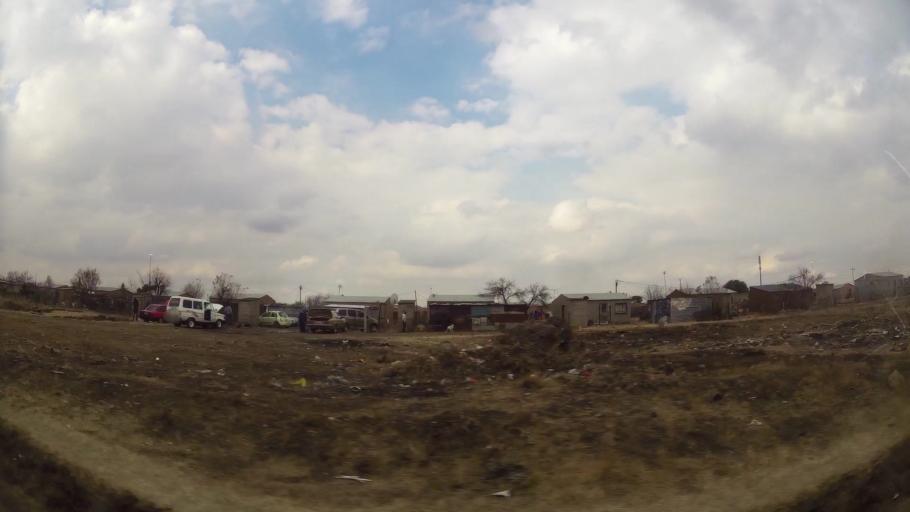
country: ZA
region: Orange Free State
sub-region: Fezile Dabi District Municipality
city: Sasolburg
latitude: -26.8530
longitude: 27.8737
